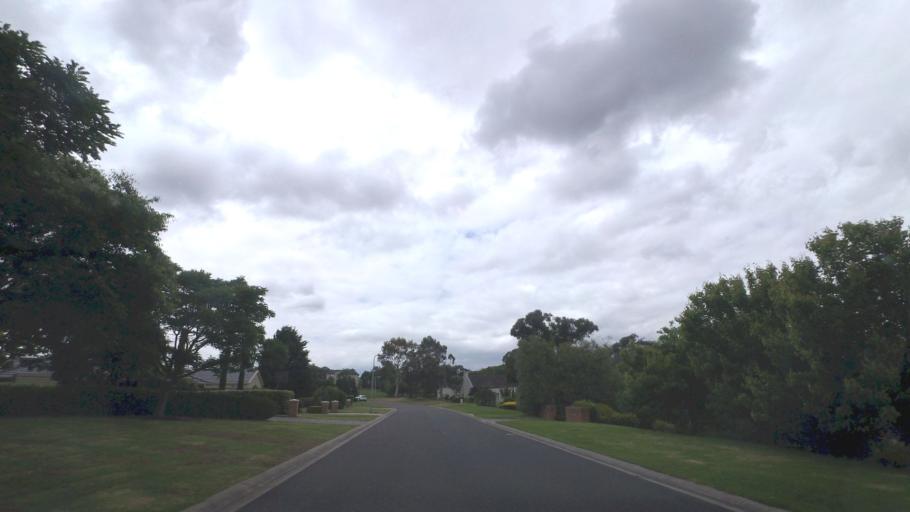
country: AU
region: Victoria
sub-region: Maroondah
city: Warranwood
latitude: -37.7719
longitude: 145.2368
